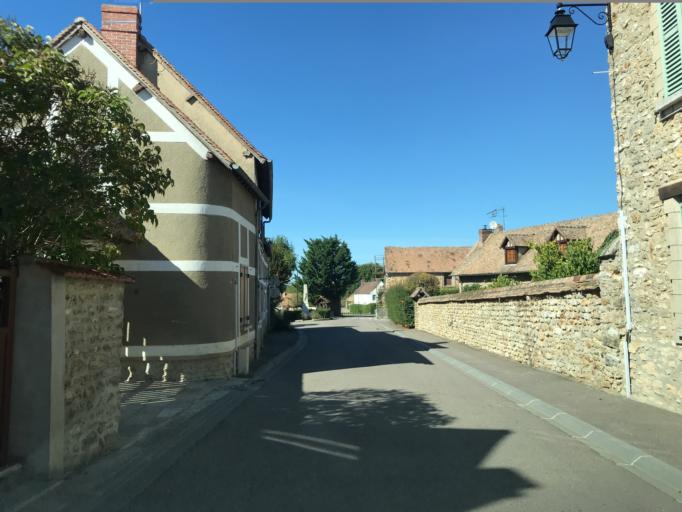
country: FR
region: Haute-Normandie
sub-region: Departement de l'Eure
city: Houlbec-Cocherel
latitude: 49.0958
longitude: 1.3375
